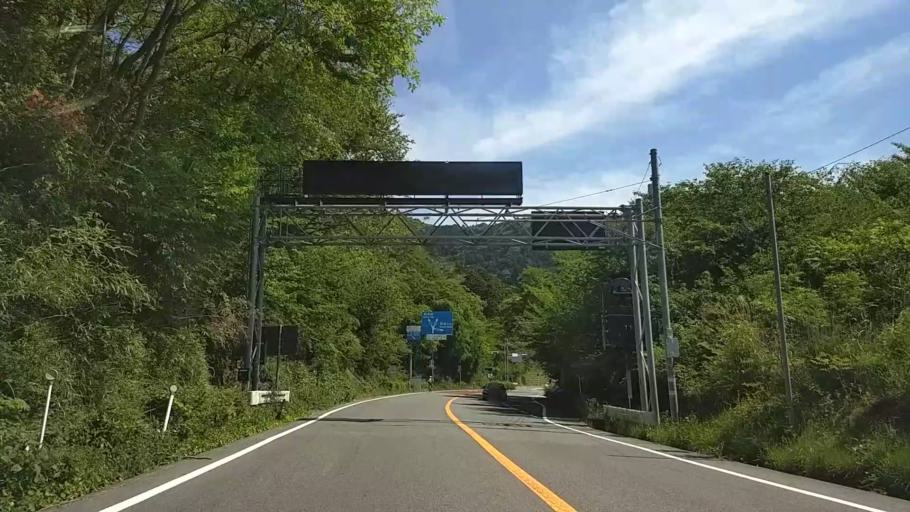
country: JP
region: Shizuoka
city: Atami
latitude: 35.1134
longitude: 139.0475
